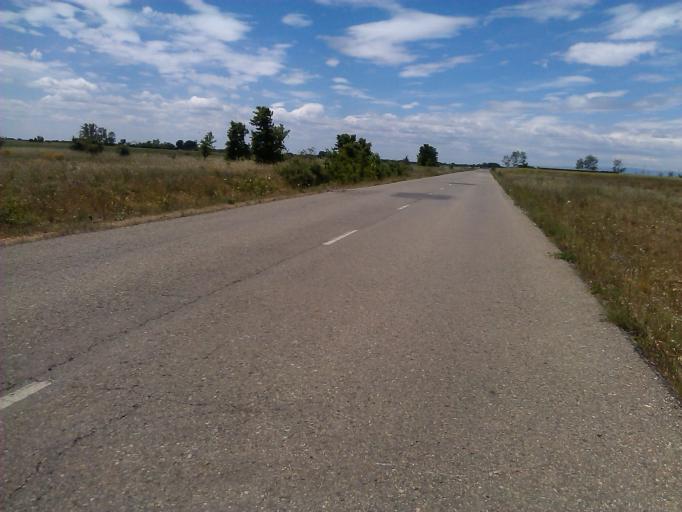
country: ES
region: Castille and Leon
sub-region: Provincia de Leon
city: Chozas de Abajo
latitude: 42.5054
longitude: -5.6933
